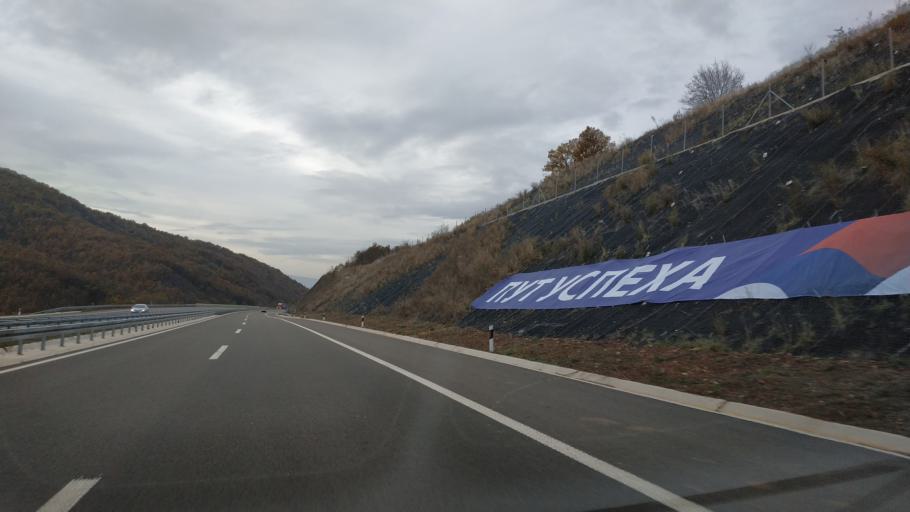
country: RS
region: Central Serbia
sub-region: Nisavski Okrug
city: Gadzin Han
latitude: 43.2896
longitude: 22.1079
